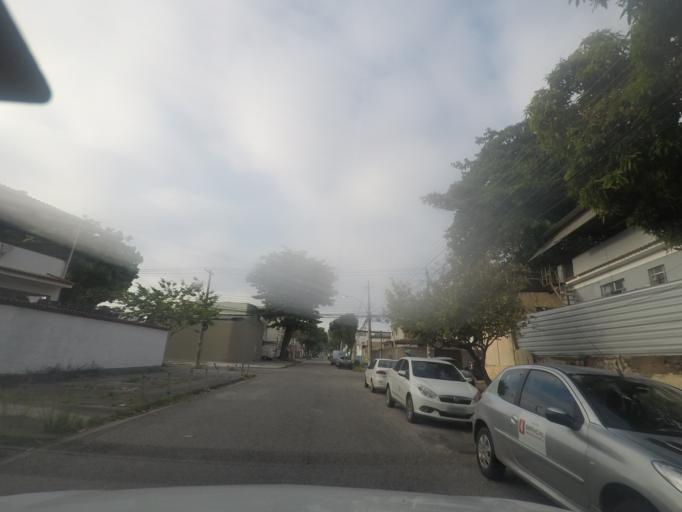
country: BR
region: Rio de Janeiro
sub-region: Duque De Caxias
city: Duque de Caxias
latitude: -22.8329
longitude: -43.2727
